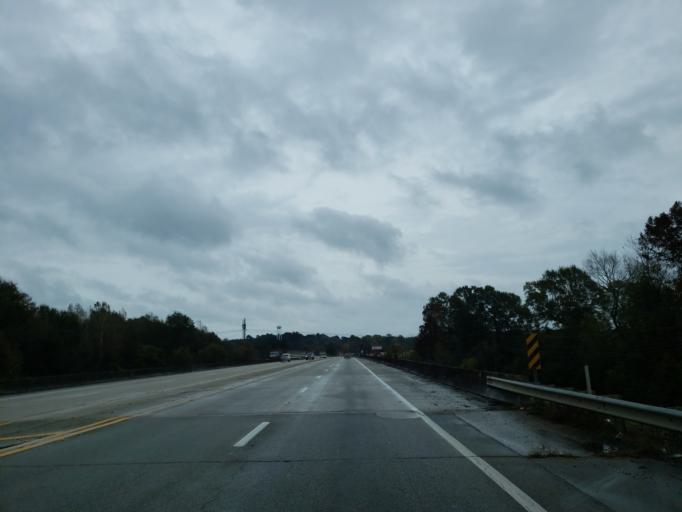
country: US
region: Mississippi
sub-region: Jones County
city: Laurel
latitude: 31.6974
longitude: -89.1106
